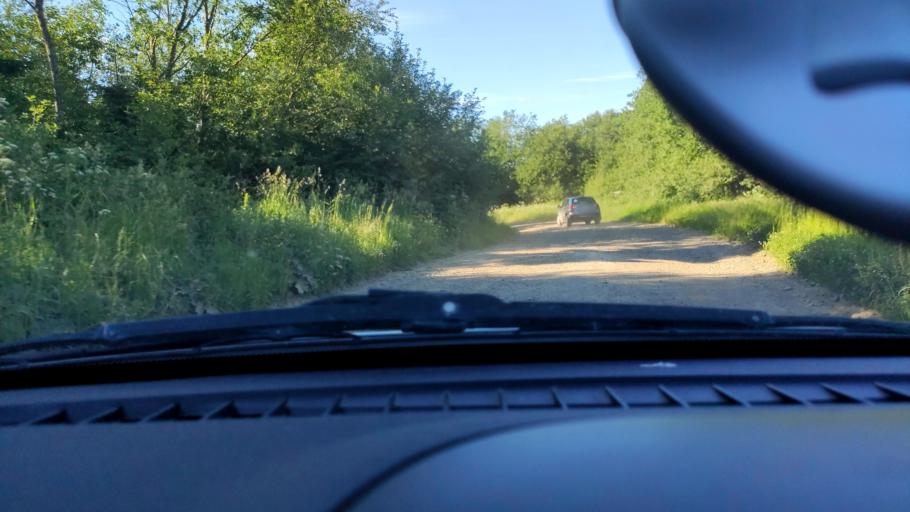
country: RU
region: Perm
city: Bershet'
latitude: 57.6941
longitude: 56.4021
